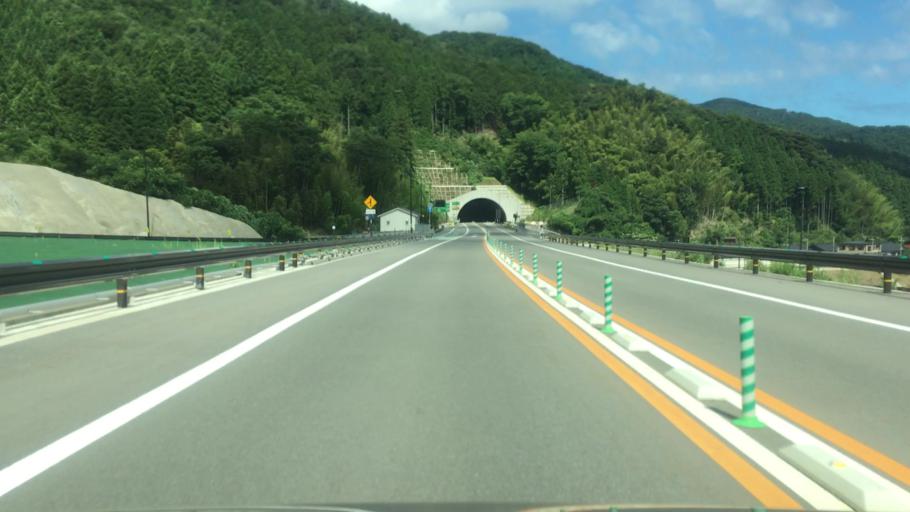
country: JP
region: Hyogo
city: Toyooka
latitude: 35.6382
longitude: 134.5659
